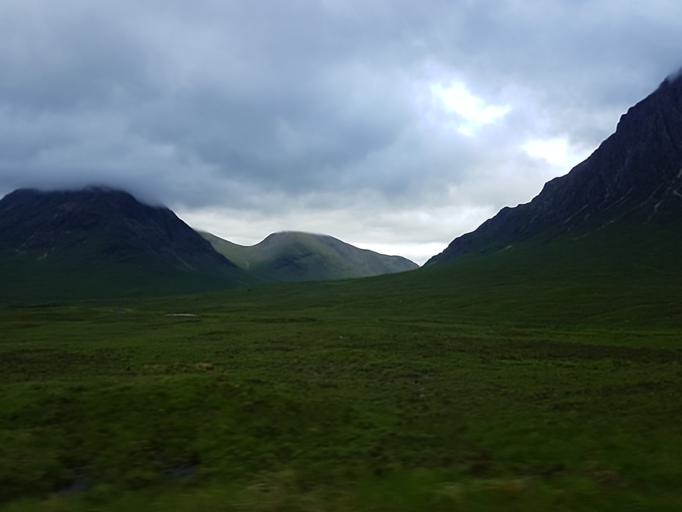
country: GB
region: Scotland
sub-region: Highland
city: Spean Bridge
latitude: 56.6562
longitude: -4.8693
